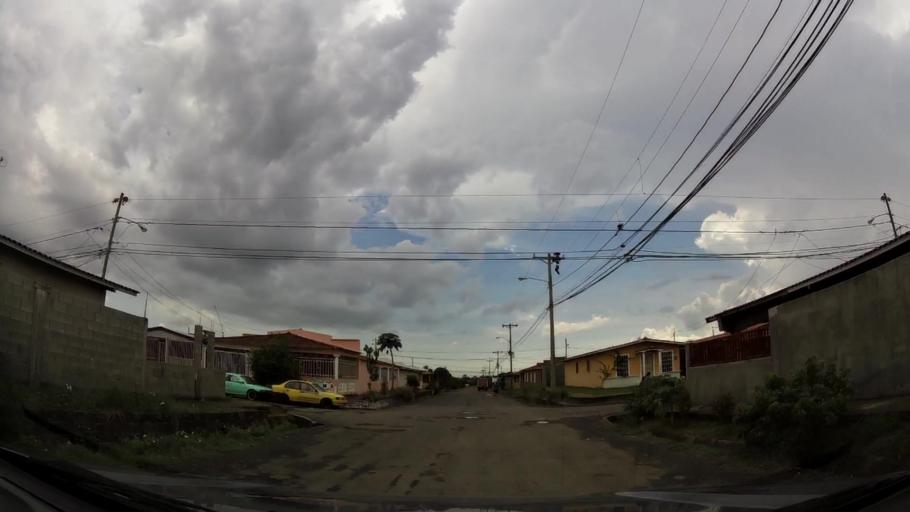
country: PA
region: Panama
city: Cabra Numero Uno
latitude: 9.1125
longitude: -79.3170
